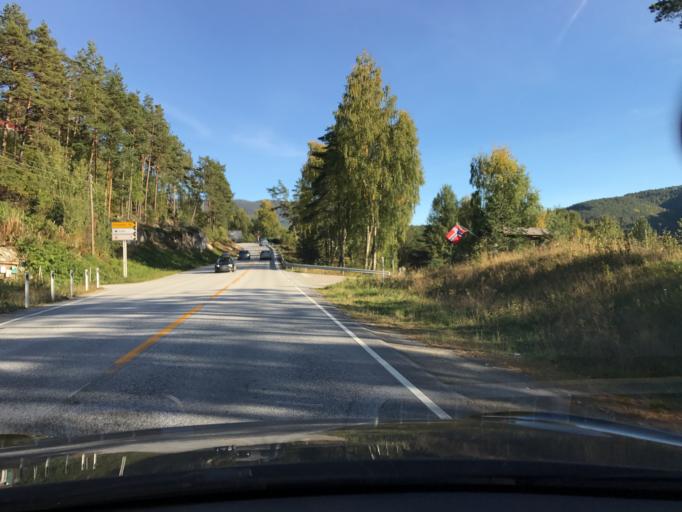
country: NO
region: Sogn og Fjordane
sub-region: Sogndal
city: Sogndalsfjora
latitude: 61.2065
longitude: 7.1669
